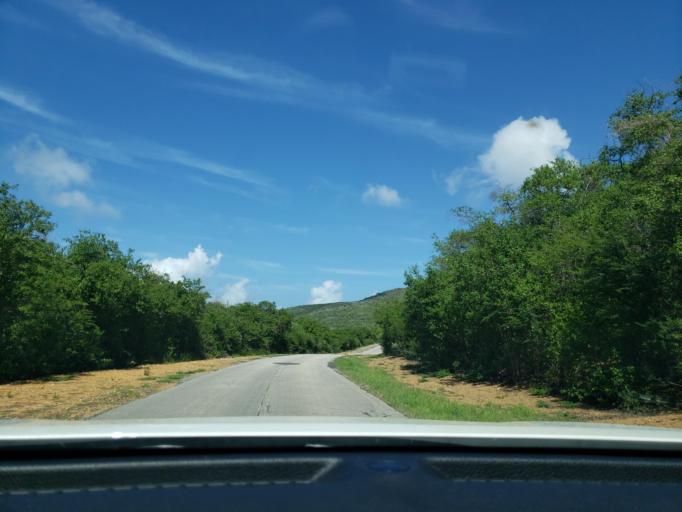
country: CW
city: Dorp Soto
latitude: 12.3476
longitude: -69.1531
